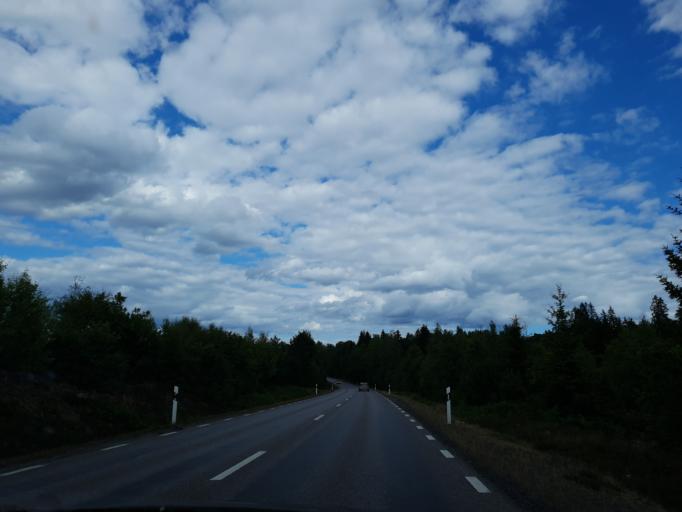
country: SE
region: Kalmar
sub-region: Emmaboda Kommun
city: Emmaboda
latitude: 56.6226
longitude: 15.5846
